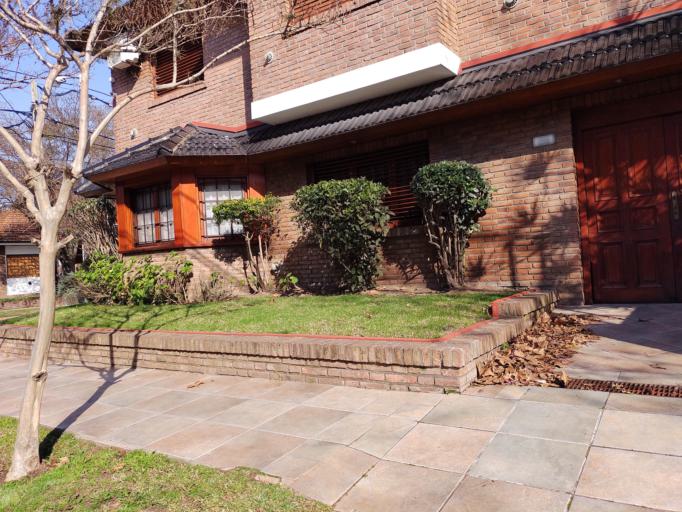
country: AR
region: Buenos Aires
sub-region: Partido de San Isidro
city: San Isidro
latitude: -34.4505
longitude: -58.5349
